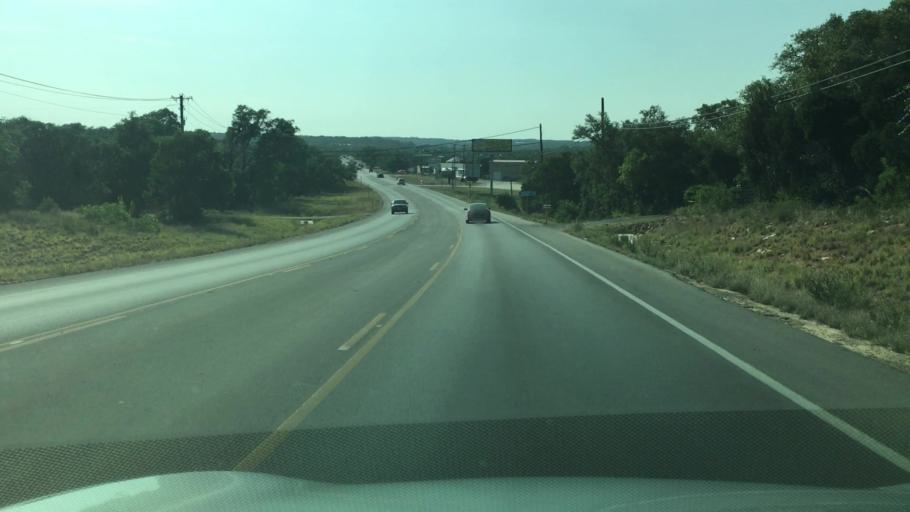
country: US
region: Texas
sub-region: Hays County
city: Wimberley
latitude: 29.9283
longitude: -98.0681
